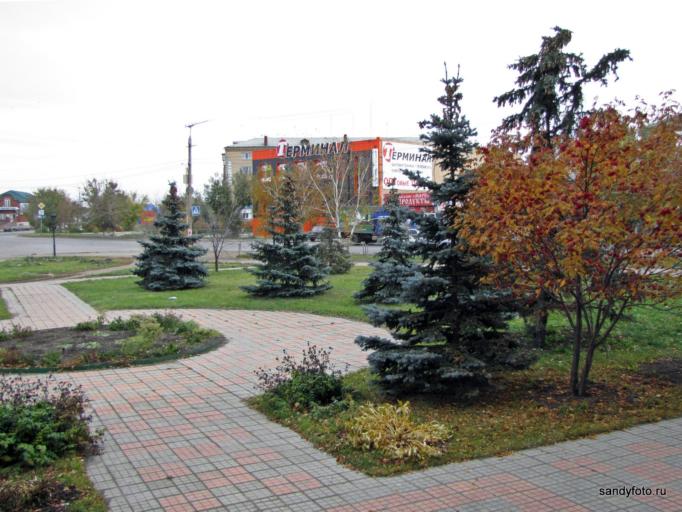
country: RU
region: Chelyabinsk
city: Troitsk
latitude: 54.0905
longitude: 61.5639
